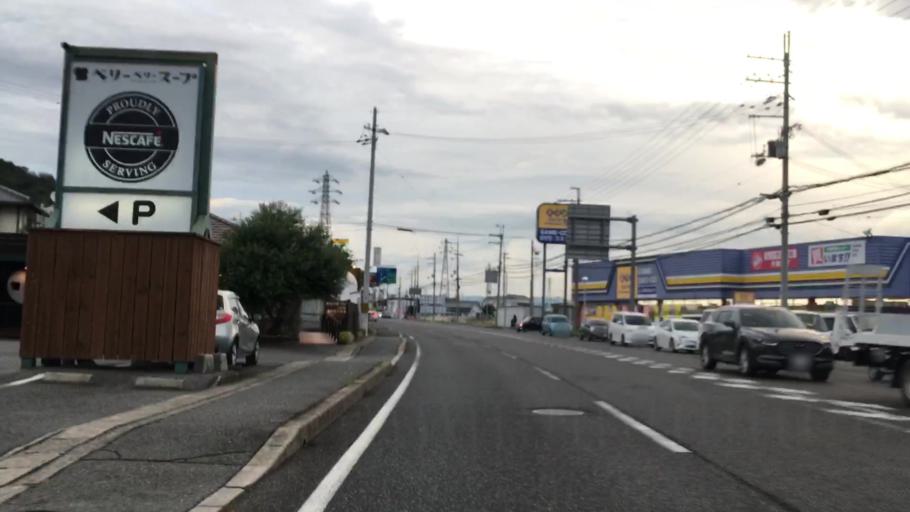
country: JP
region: Hyogo
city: Himeji
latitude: 34.8688
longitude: 134.7289
